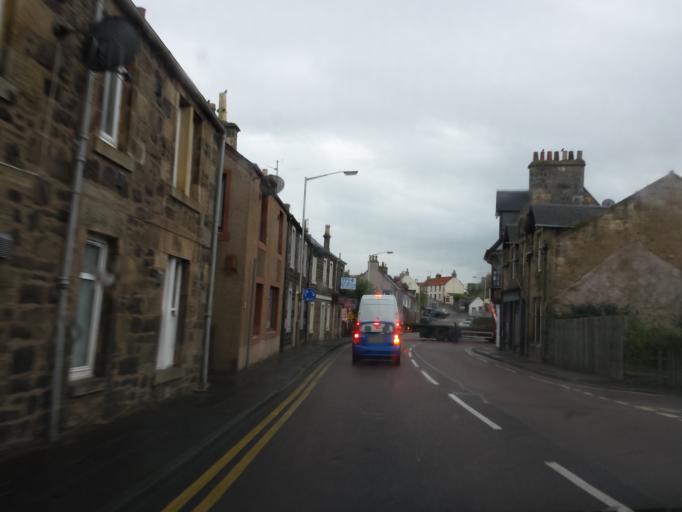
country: GB
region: Scotland
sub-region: Fife
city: Leuchars
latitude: 56.3828
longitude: -2.8878
